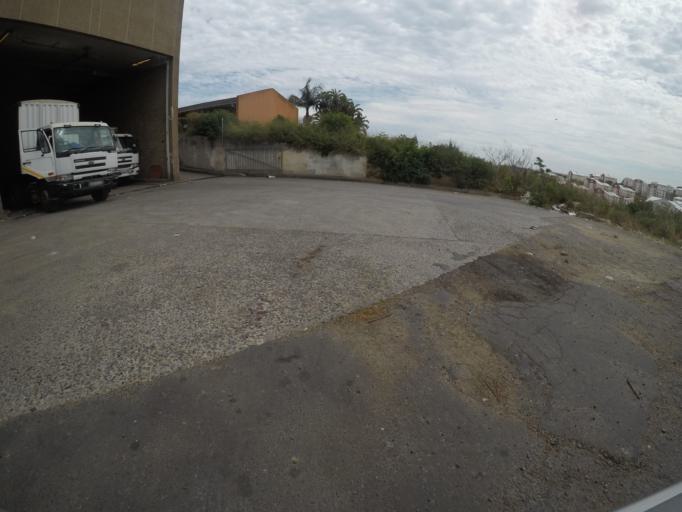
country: ZA
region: Eastern Cape
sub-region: Buffalo City Metropolitan Municipality
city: East London
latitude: -32.9943
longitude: 27.8663
